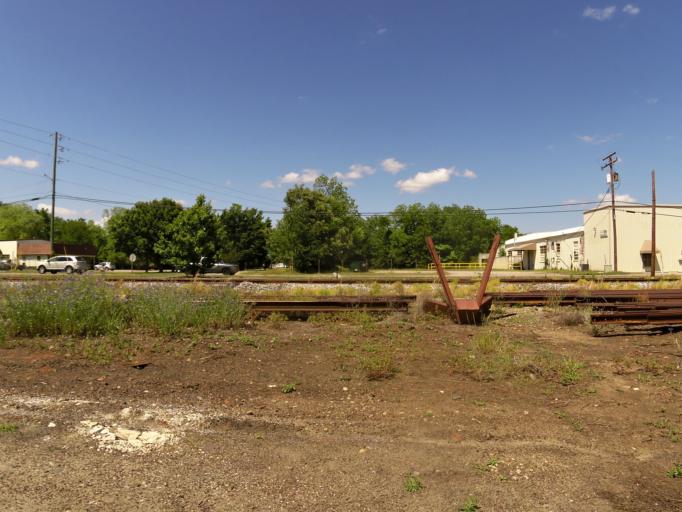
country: US
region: South Carolina
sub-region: Aiken County
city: Aiken
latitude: 33.5543
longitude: -81.7076
